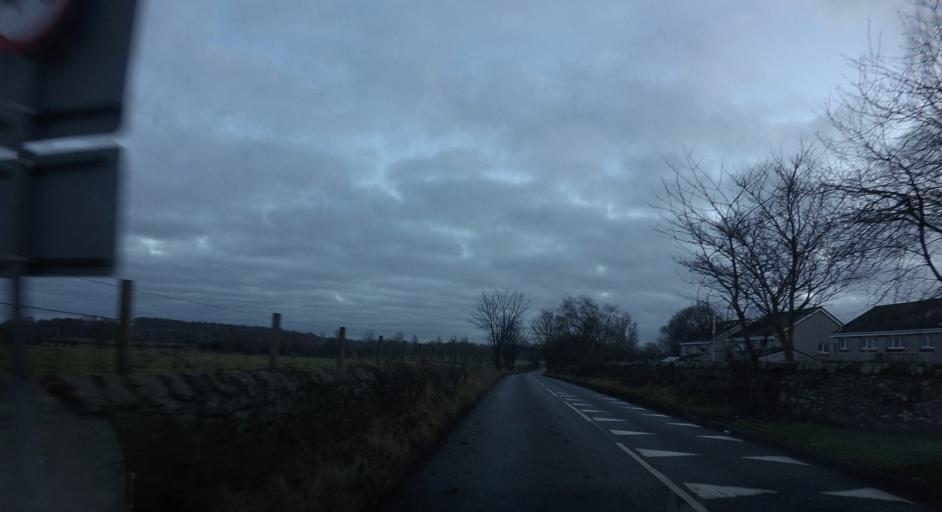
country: GB
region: Scotland
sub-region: Fife
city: Crossford
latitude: 56.0584
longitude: -3.4931
